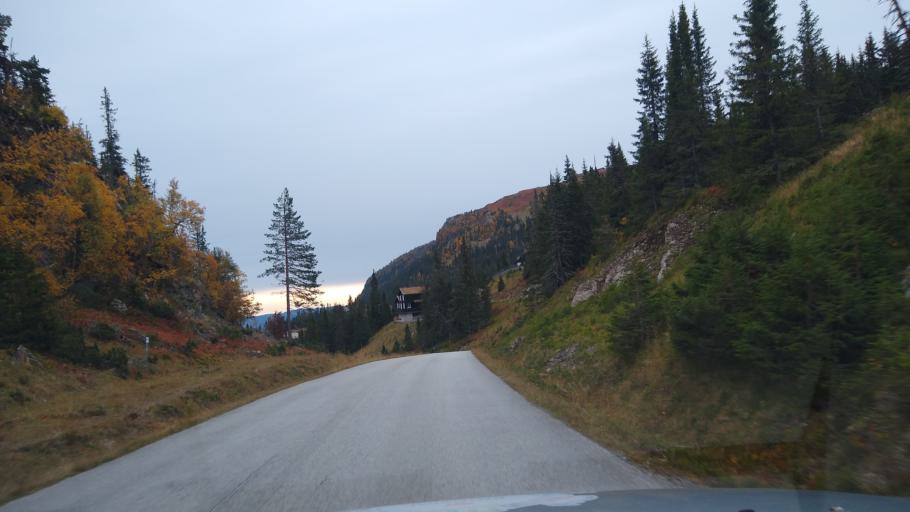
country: NO
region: Oppland
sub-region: Ringebu
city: Ringebu
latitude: 61.4780
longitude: 10.1258
